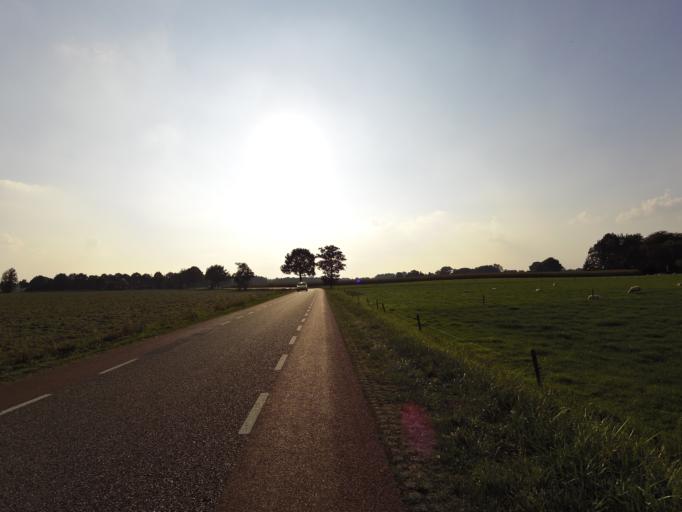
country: NL
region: Gelderland
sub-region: Gemeente Aalten
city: Aalten
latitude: 51.9092
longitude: 6.5211
